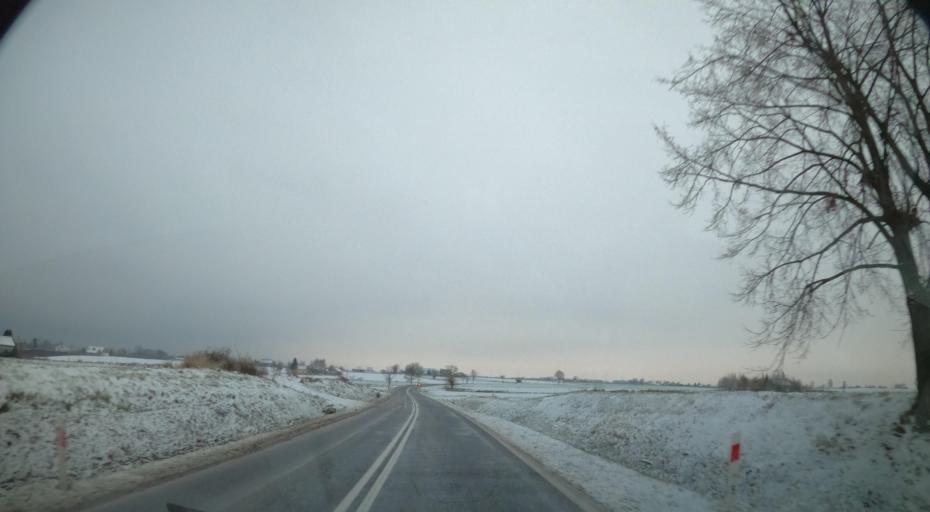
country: PL
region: Kujawsko-Pomorskie
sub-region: Powiat lipnowski
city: Dobrzyn nad Wisla
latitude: 52.6361
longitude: 19.4053
